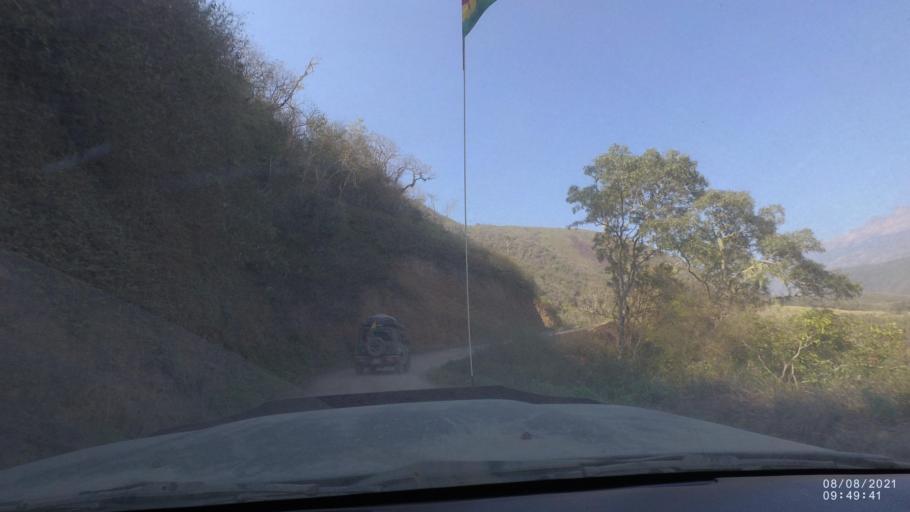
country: BO
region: La Paz
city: Quime
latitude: -16.6181
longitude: -66.7286
